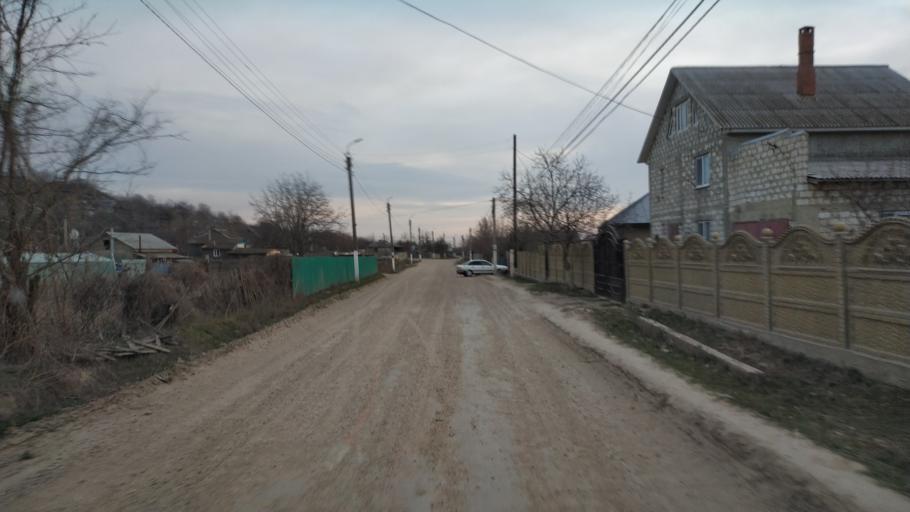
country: MD
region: Hincesti
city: Dancu
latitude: 46.7524
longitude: 28.2066
